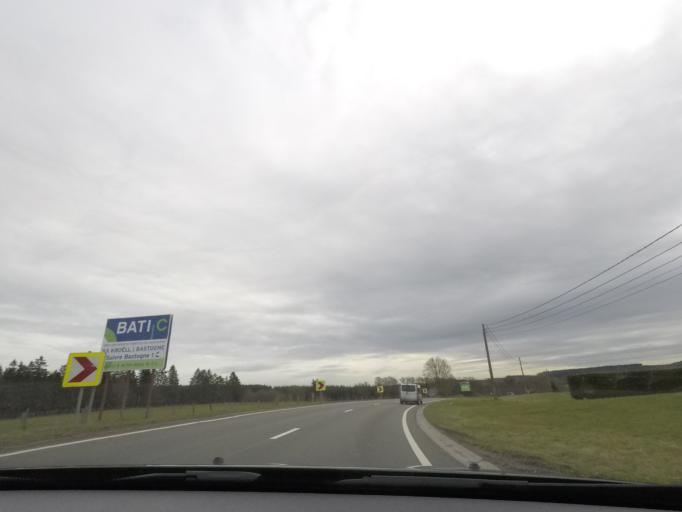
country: BE
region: Wallonia
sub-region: Province du Luxembourg
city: Bastogne
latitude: 49.9895
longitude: 5.7550
